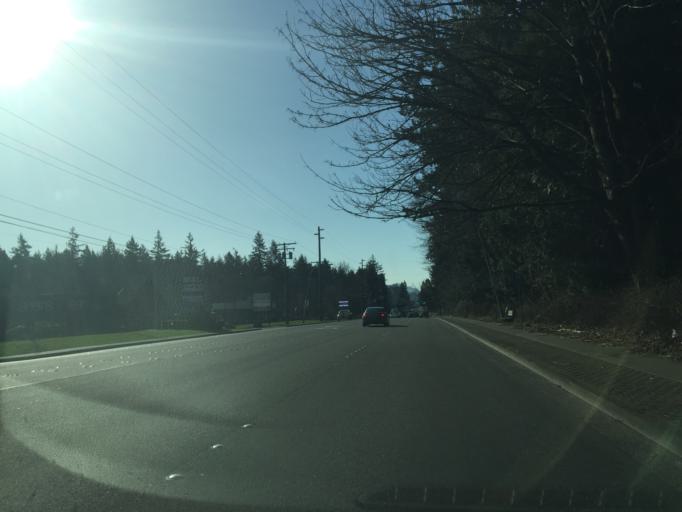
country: US
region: Washington
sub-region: Whatcom County
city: Bellingham
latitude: 48.7789
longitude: -122.4862
